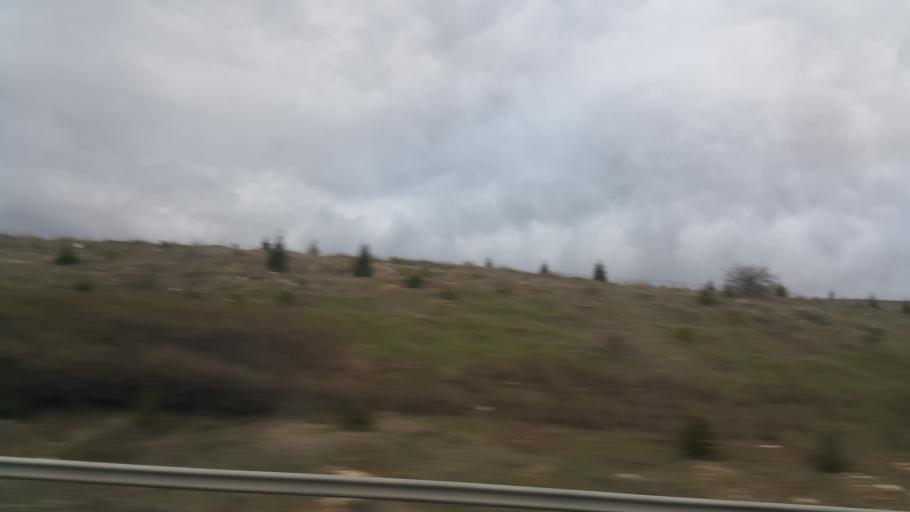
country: TR
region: Ankara
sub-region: Goelbasi
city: Golbasi
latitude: 39.7872
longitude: 32.6635
